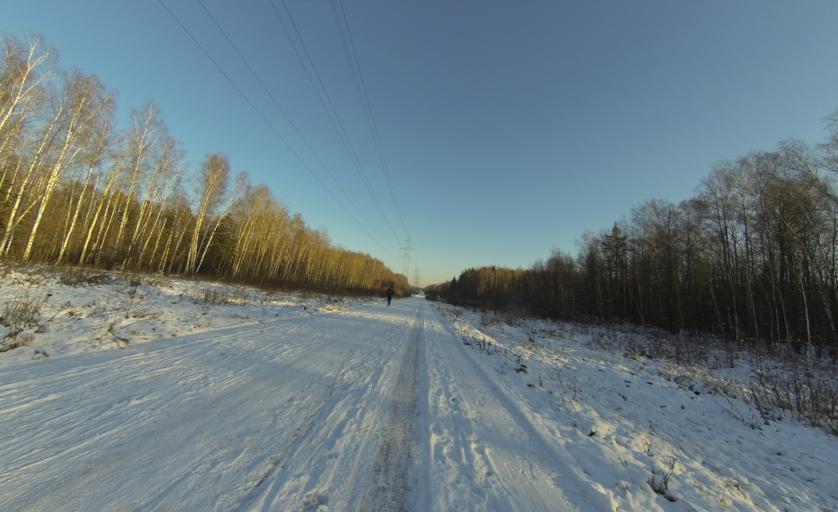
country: RU
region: Moscow
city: Babushkin
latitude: 55.8425
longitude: 37.7344
